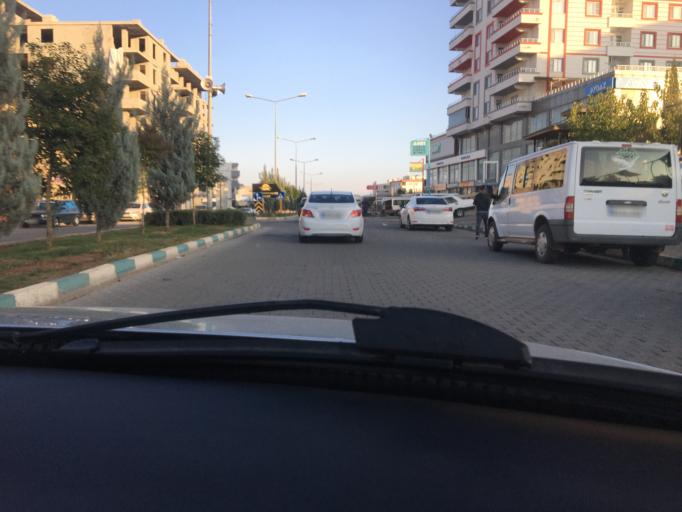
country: TR
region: Sanliurfa
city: Halfeti
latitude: 37.2310
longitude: 37.9455
